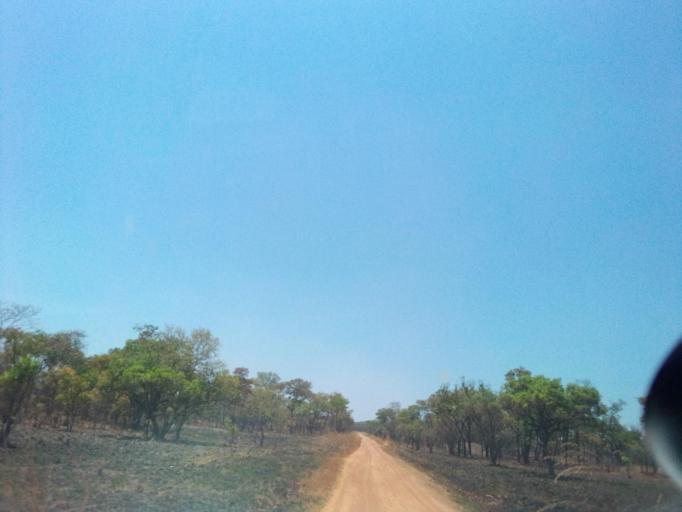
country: ZM
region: Northern
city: Mpika
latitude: -12.2542
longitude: 30.6882
